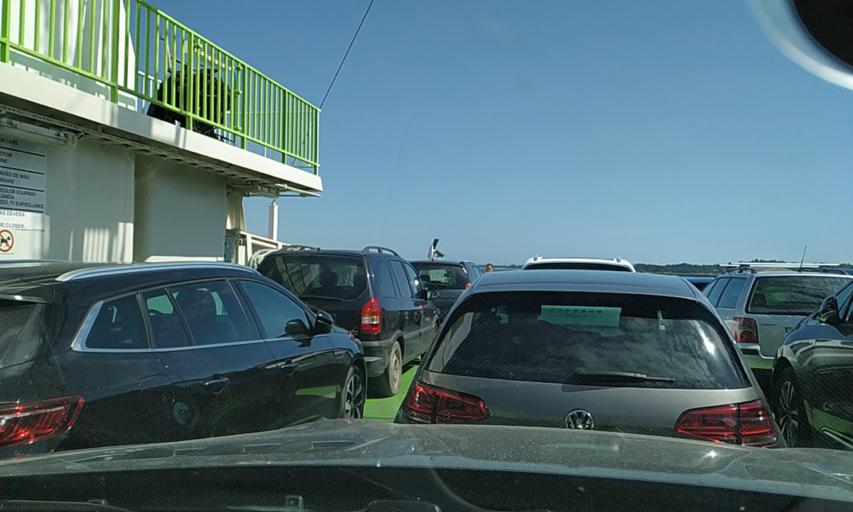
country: PT
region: Setubal
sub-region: Setubal
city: Setubal
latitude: 38.4822
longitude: -8.8737
